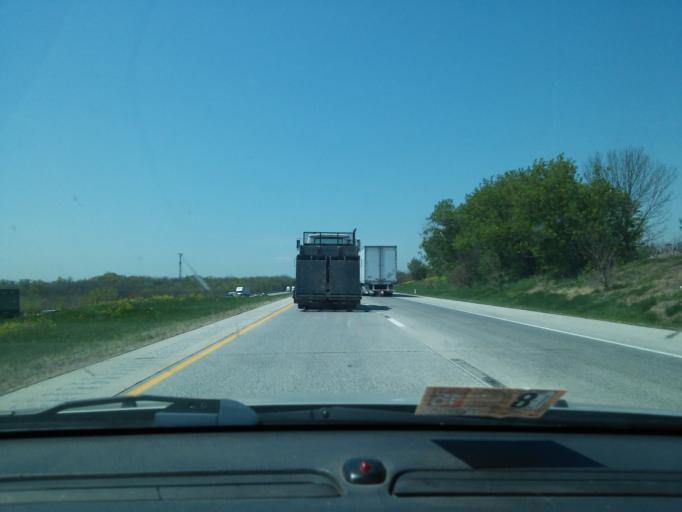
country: US
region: Pennsylvania
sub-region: Lebanon County
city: Jonestown
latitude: 40.4455
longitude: -76.4687
